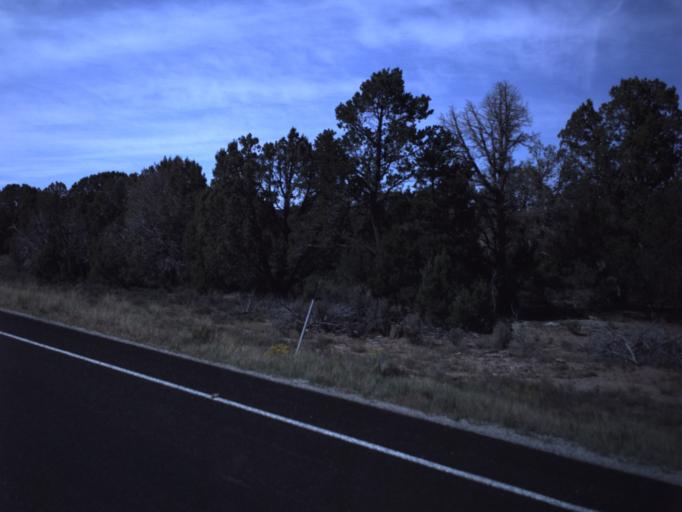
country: US
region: Utah
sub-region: San Juan County
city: Monticello
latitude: 37.8394
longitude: -109.1218
